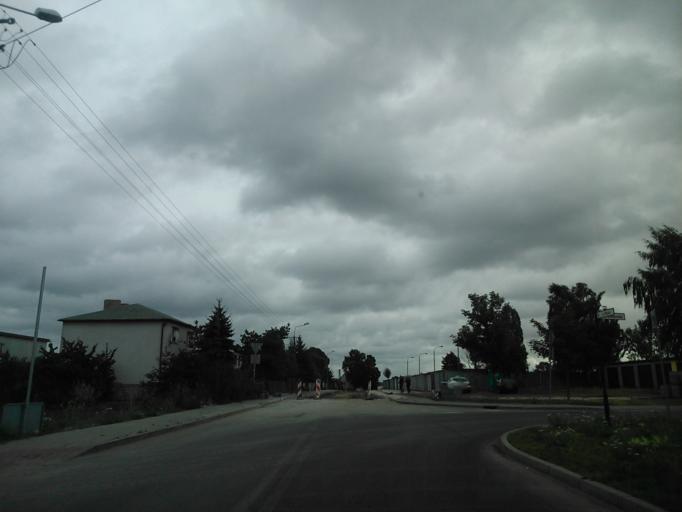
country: PL
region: Kujawsko-Pomorskie
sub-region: Powiat inowroclawski
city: Kruszwica
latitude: 52.6802
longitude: 18.3390
